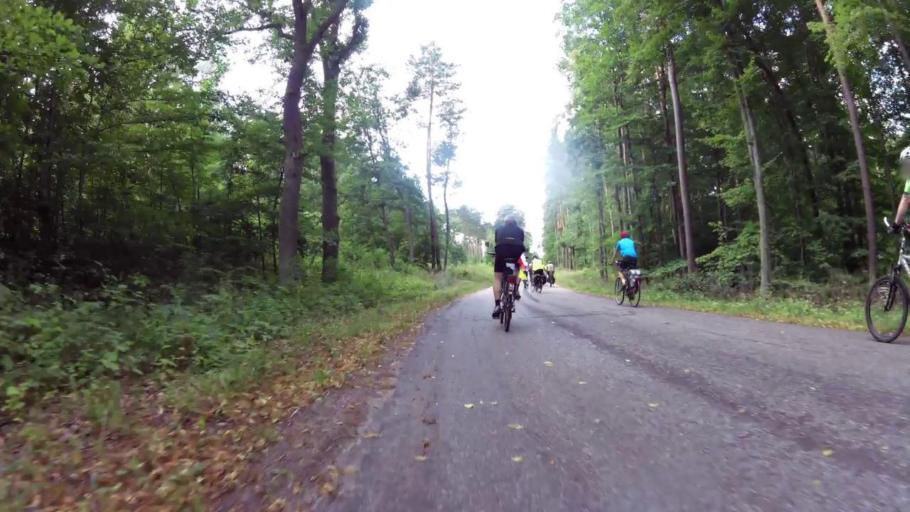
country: PL
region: West Pomeranian Voivodeship
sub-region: Powiat drawski
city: Drawsko Pomorskie
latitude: 53.4678
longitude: 15.7818
